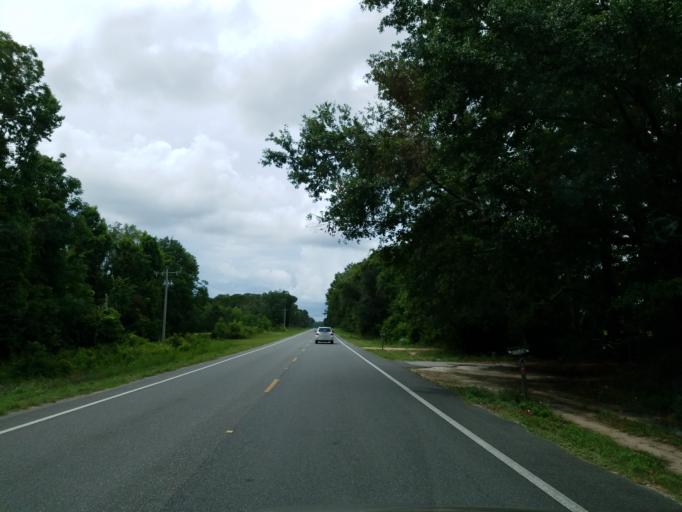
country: US
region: Florida
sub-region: Alachua County
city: High Springs
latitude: 29.9040
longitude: -82.4997
